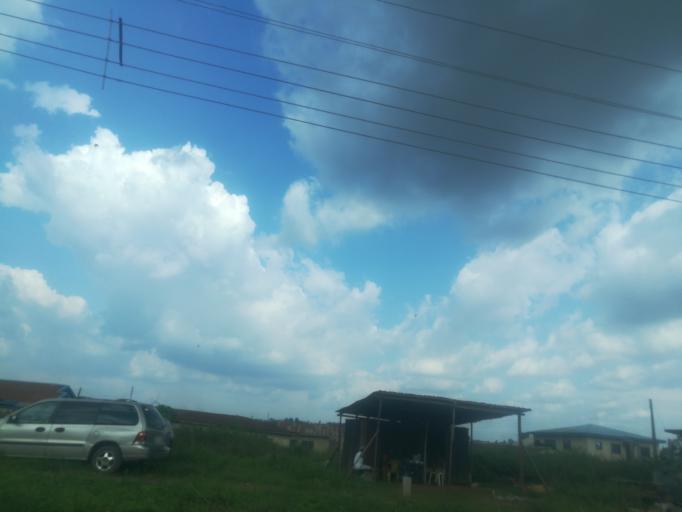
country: NG
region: Oyo
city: Ibadan
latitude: 7.3977
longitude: 3.8363
